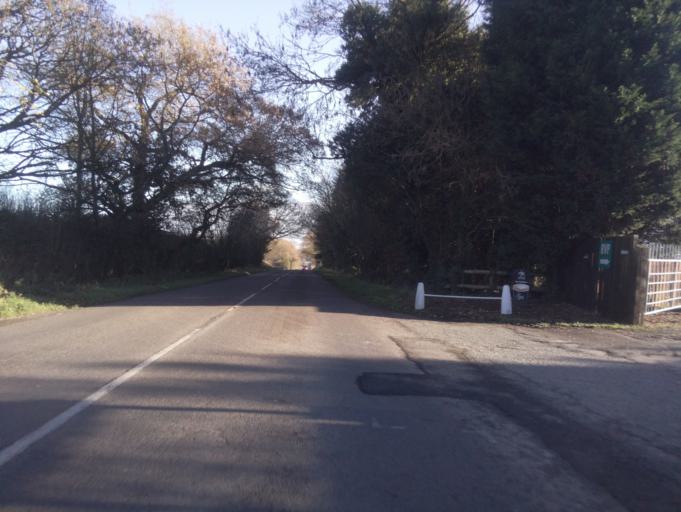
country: GB
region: England
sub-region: Staffordshire
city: Barton under Needwood
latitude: 52.8174
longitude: -1.7565
